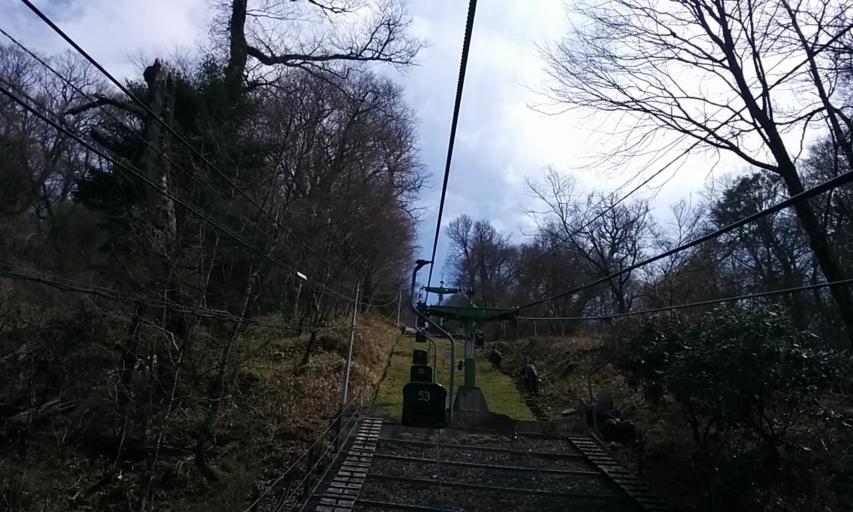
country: JP
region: Tokushima
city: Wakimachi
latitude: 33.8661
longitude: 134.0893
